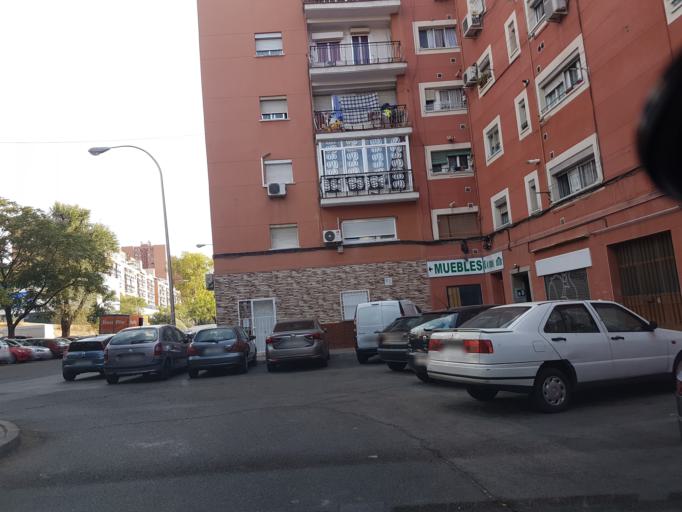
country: ES
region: Madrid
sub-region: Provincia de Madrid
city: Puente de Vallecas
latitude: 40.4039
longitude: -3.6609
